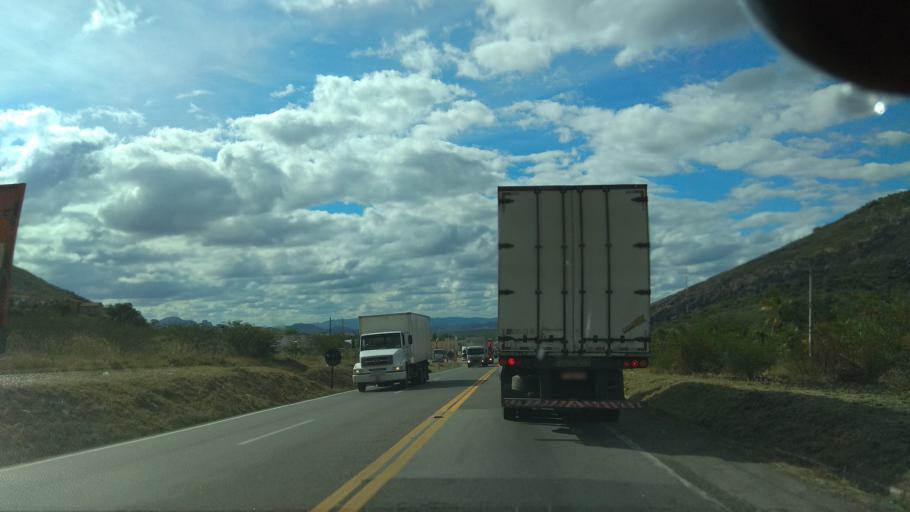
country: BR
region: Bahia
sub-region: Amargosa
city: Amargosa
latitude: -12.8813
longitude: -39.8583
